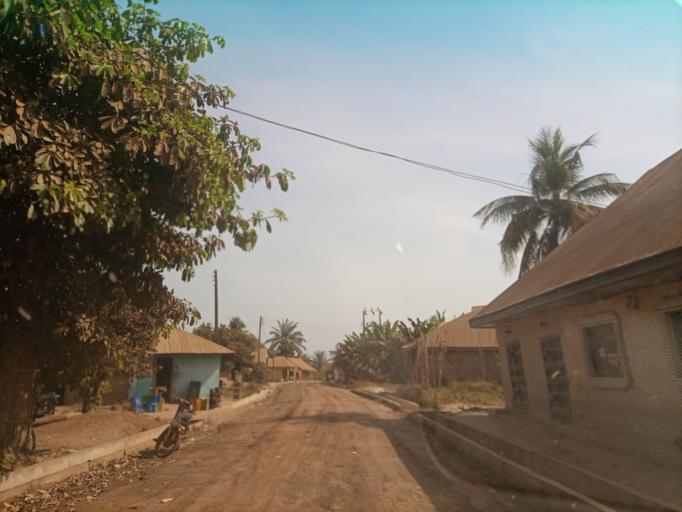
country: NG
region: Enugu
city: Eha Amufu
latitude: 6.6632
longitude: 7.7565
